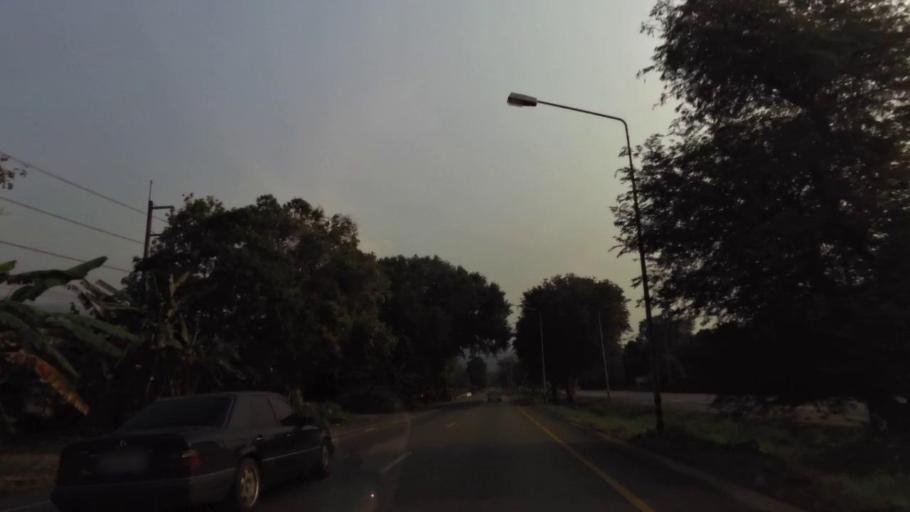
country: TH
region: Chanthaburi
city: Chanthaburi
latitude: 12.5816
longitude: 102.1585
